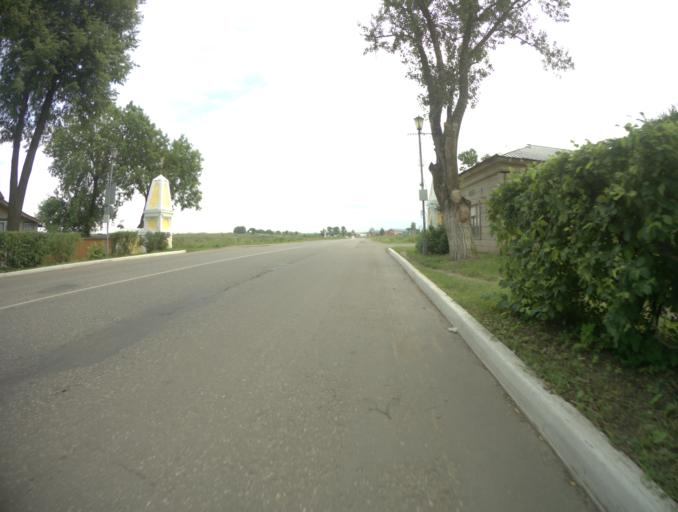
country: RU
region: Vladimir
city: Suzdal'
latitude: 56.4069
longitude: 40.4455
